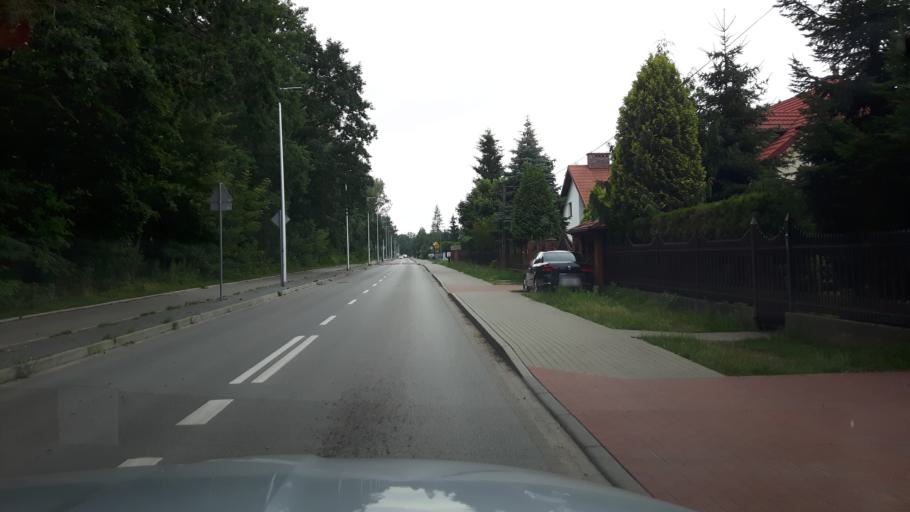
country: PL
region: Masovian Voivodeship
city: Zielonka
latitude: 52.2964
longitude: 21.1621
